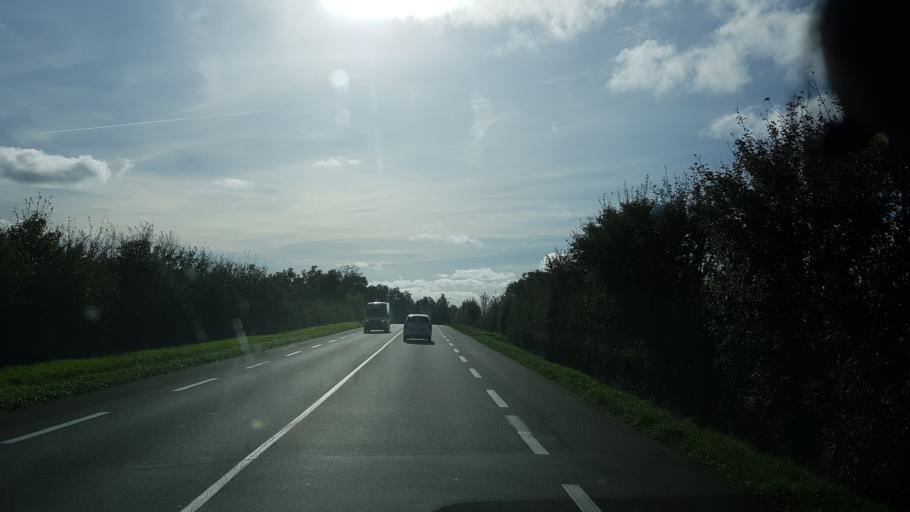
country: FR
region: Poitou-Charentes
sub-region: Departement de la Charente
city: Saint-Claud
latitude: 45.9112
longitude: 0.4924
